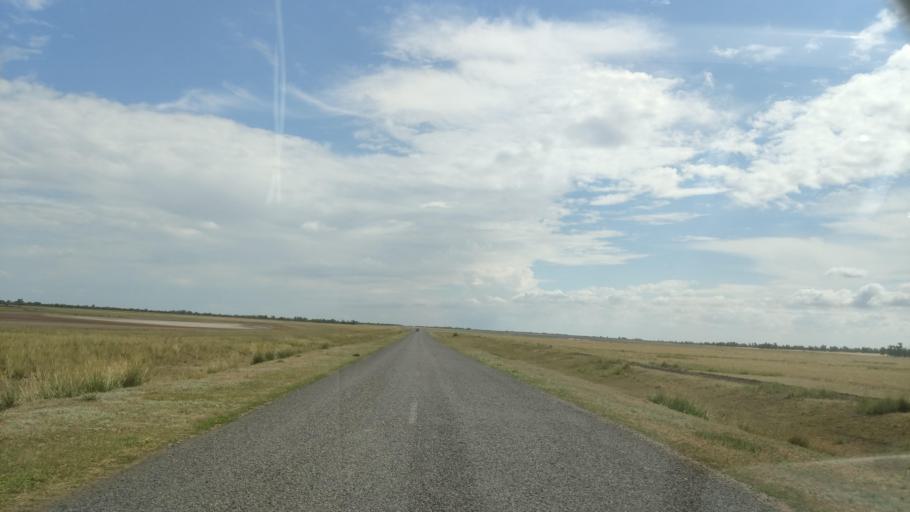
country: KZ
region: Pavlodar
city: Pavlodar
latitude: 52.6352
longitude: 76.9119
